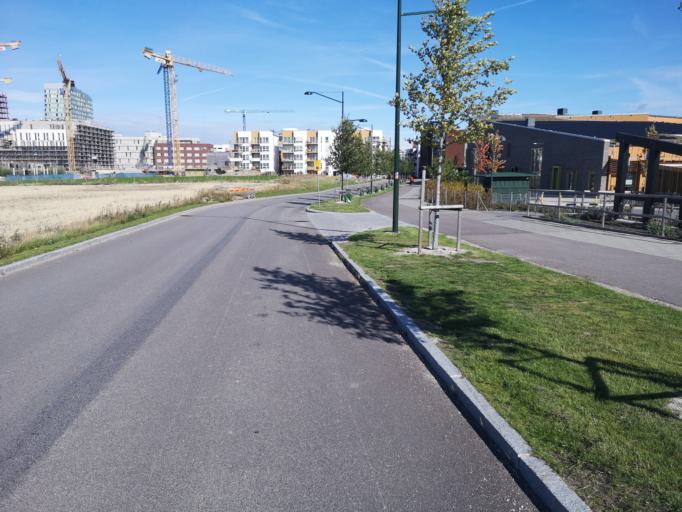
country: SE
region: Skane
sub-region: Malmo
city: Bunkeflostrand
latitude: 55.5584
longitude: 12.9786
